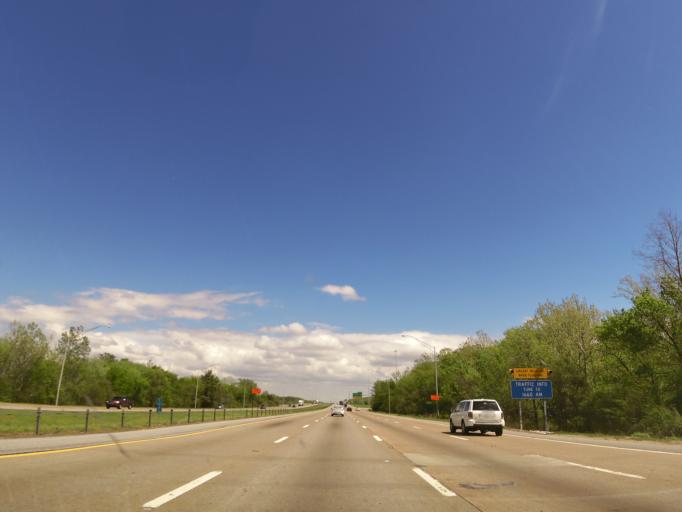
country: US
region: Tennessee
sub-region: Shelby County
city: Memphis
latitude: 35.1921
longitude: -89.9846
